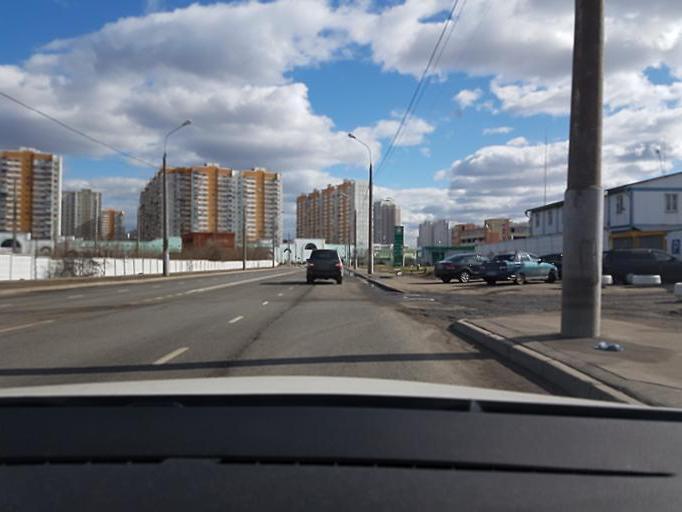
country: RU
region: Moskovskaya
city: Pavshino
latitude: 55.8354
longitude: 37.3475
